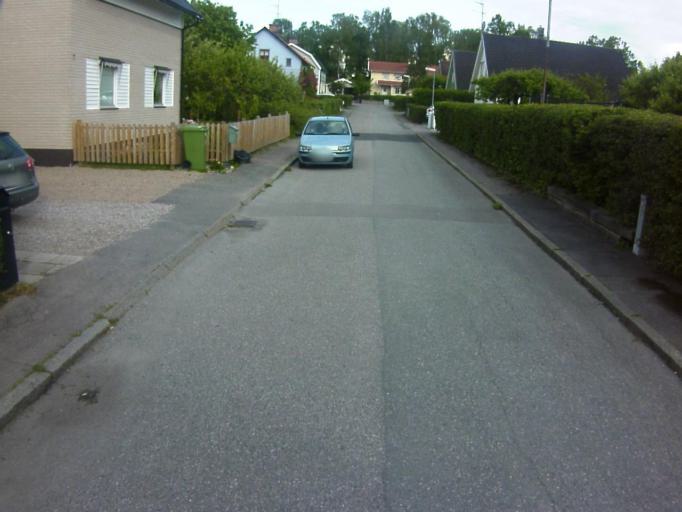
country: SE
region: Soedermanland
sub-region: Eskilstuna Kommun
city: Eskilstuna
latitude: 59.3564
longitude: 16.5112
